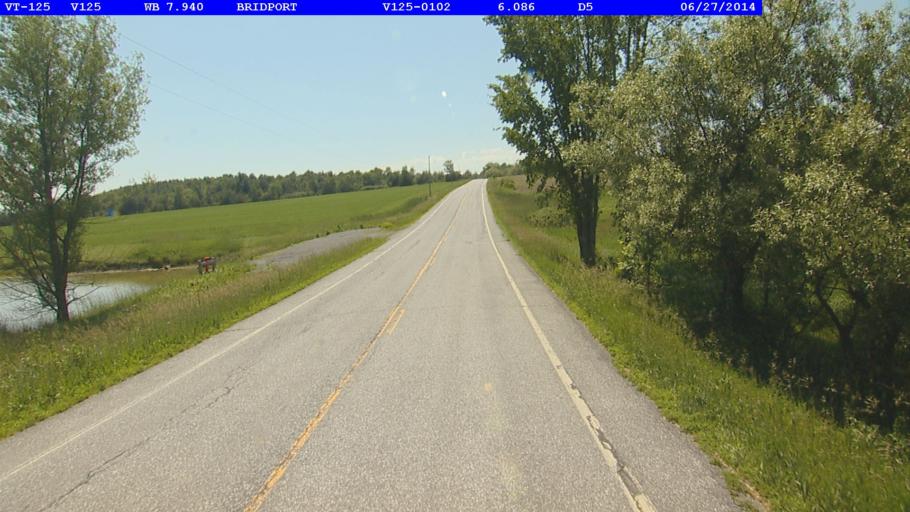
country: US
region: Vermont
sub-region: Addison County
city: Middlebury (village)
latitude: 43.9903
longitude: -73.2960
